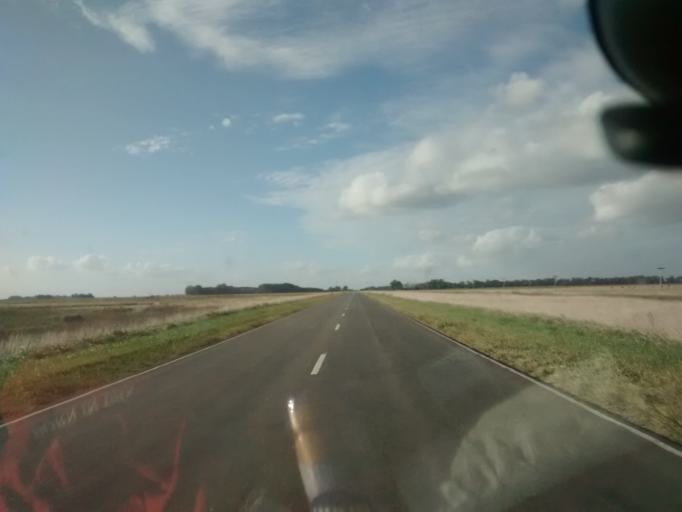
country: AR
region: Buenos Aires
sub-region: Partido de Ayacucho
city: Ayacucho
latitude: -36.6777
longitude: -58.5748
